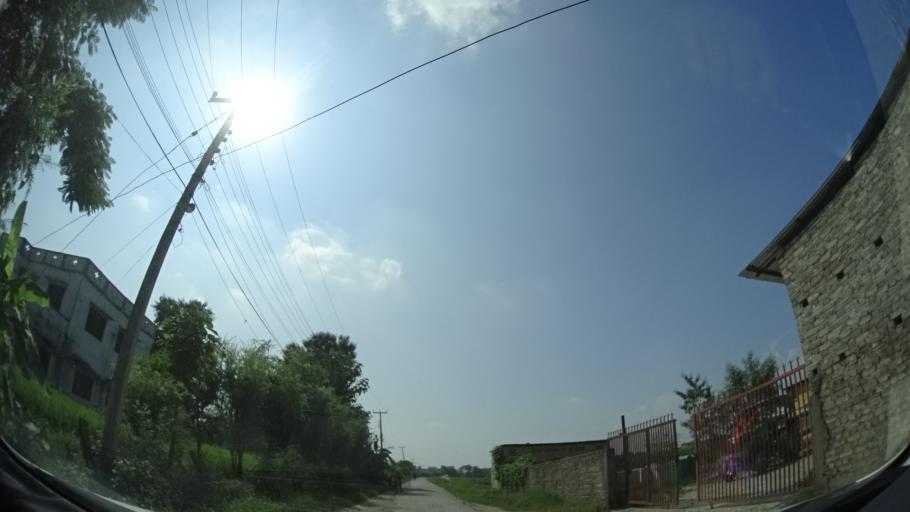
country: NP
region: Western Region
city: Butwal
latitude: 27.6218
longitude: 83.4740
